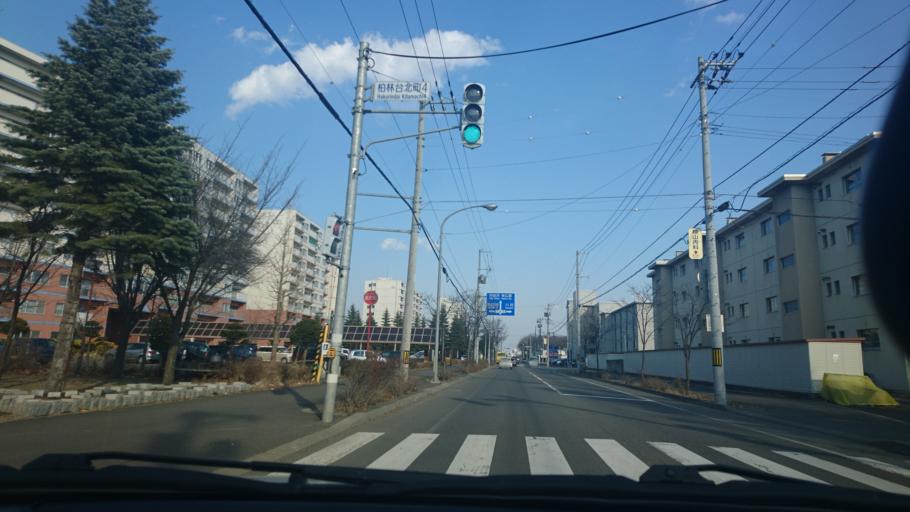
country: JP
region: Hokkaido
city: Obihiro
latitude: 42.9252
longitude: 143.1684
